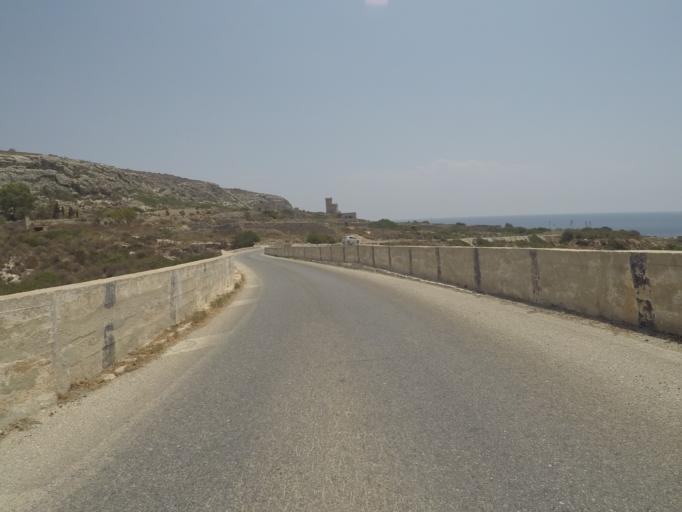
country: MT
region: Is-Siggiewi
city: Siggiewi
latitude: 35.8315
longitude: 14.4199
